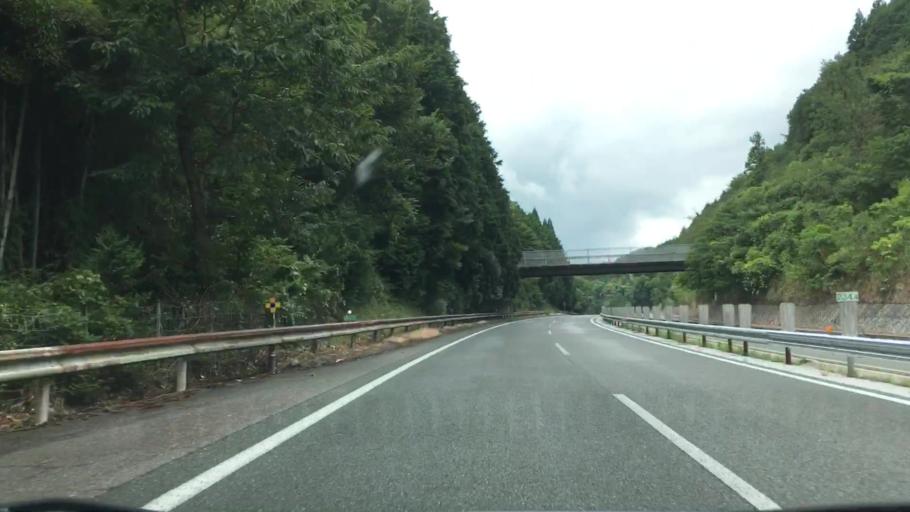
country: JP
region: Okayama
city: Niimi
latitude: 34.9683
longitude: 133.3501
